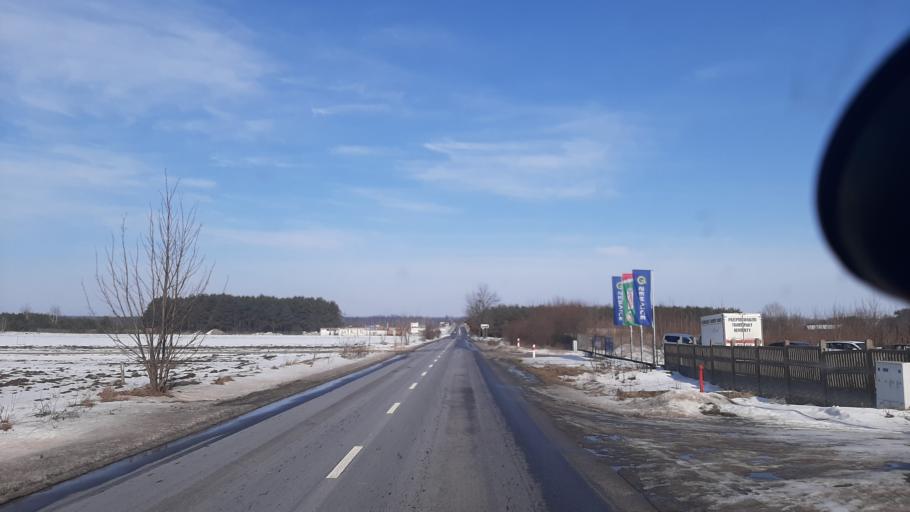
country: PL
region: Lublin Voivodeship
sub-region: Powiat pulawski
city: Kurow
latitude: 51.3992
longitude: 22.1996
